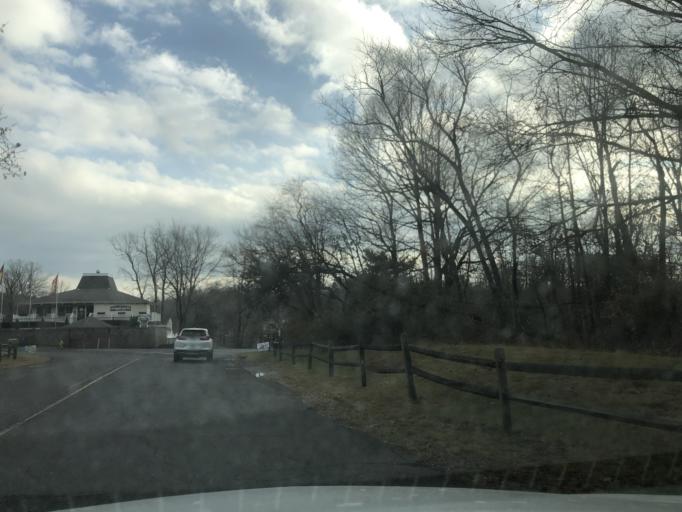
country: US
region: New Jersey
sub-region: Camden County
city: Glendora
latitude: 39.8253
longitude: -75.0790
